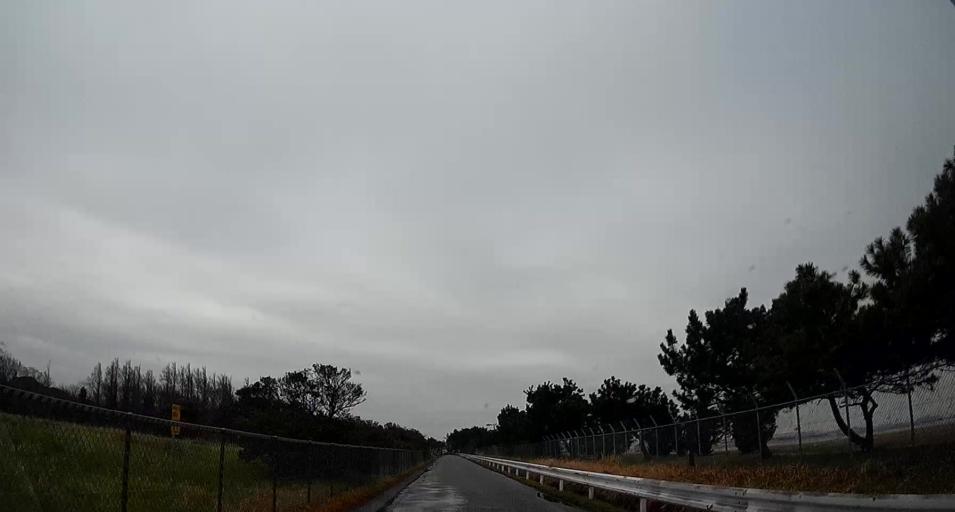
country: JP
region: Chiba
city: Kisarazu
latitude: 35.4067
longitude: 139.9133
